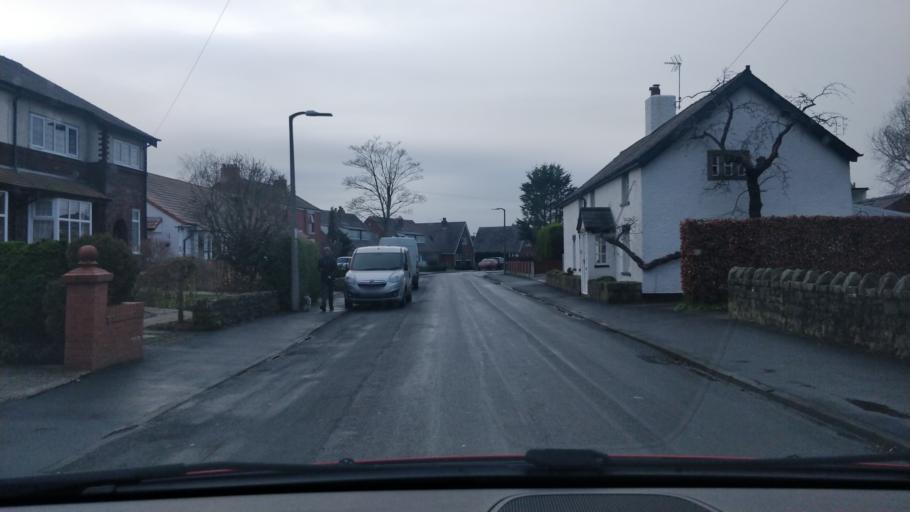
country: GB
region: England
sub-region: Lancashire
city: Preston
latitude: 53.7453
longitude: -2.7321
